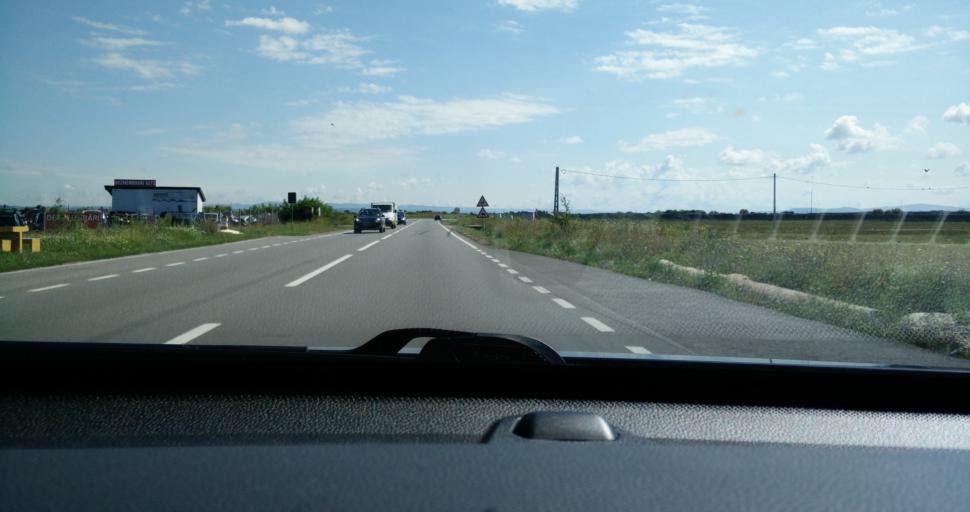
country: RO
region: Bihor
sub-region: Comuna Osorheiu
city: Osorheiu
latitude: 47.0516
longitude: 22.0605
